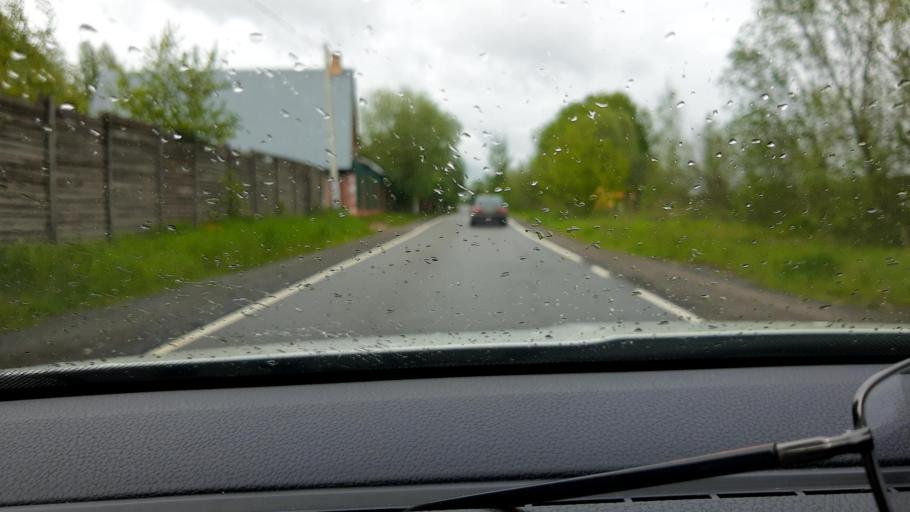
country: RU
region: Moskovskaya
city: Nikolina Gora
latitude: 55.7519
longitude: 36.9779
